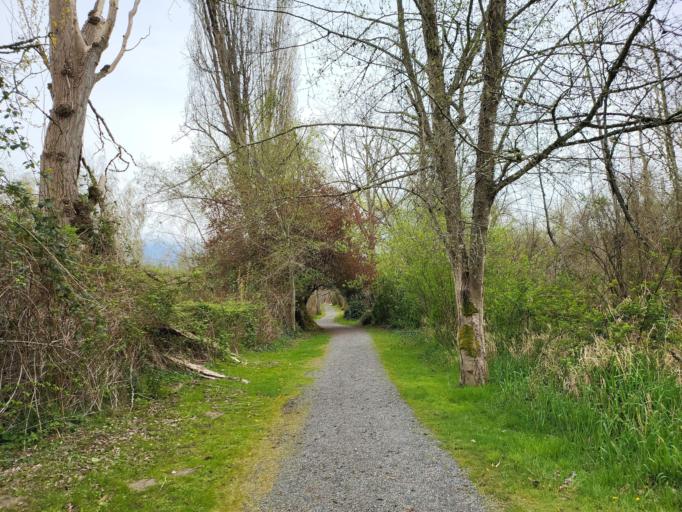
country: US
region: Washington
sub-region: King County
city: Newport
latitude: 47.5886
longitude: -122.1901
